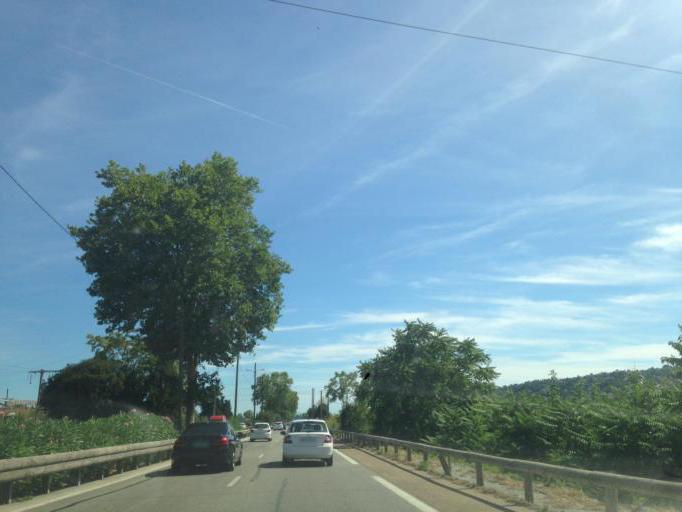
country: FR
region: Provence-Alpes-Cote d'Azur
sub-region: Departement des Alpes-Maritimes
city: La Gaude
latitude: 43.7195
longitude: 7.1863
